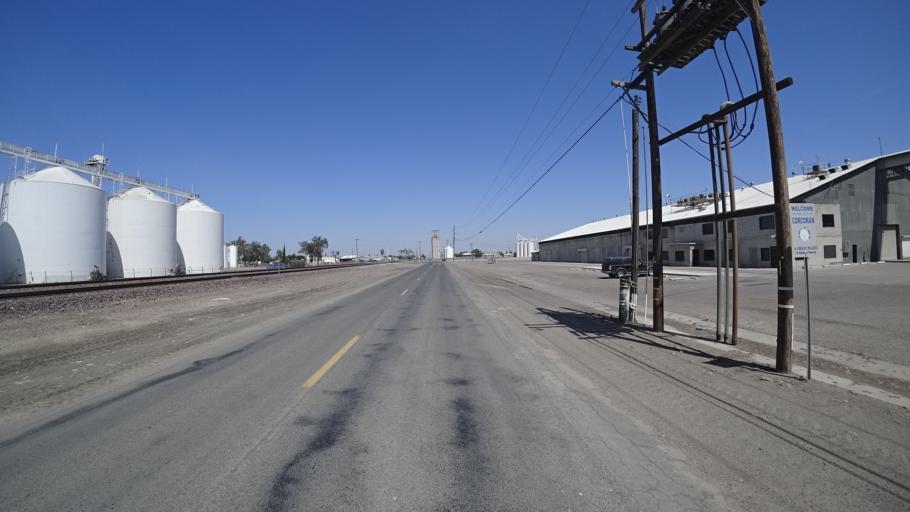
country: US
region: California
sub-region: Kings County
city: Corcoran
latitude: 36.0929
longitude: -119.5526
